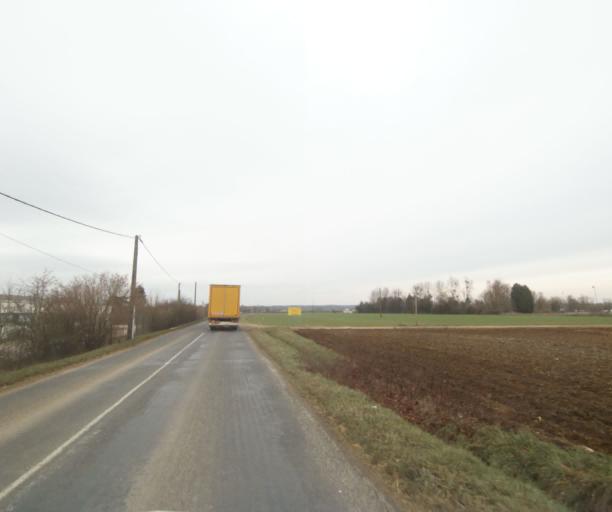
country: FR
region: Champagne-Ardenne
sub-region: Departement de la Haute-Marne
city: Villiers-en-Lieu
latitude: 48.6514
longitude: 4.9069
